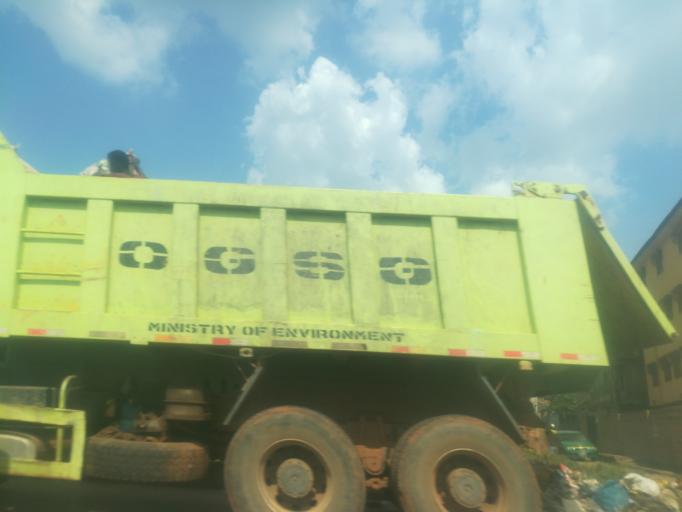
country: NG
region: Ogun
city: Abeokuta
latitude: 7.1713
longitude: 3.3580
